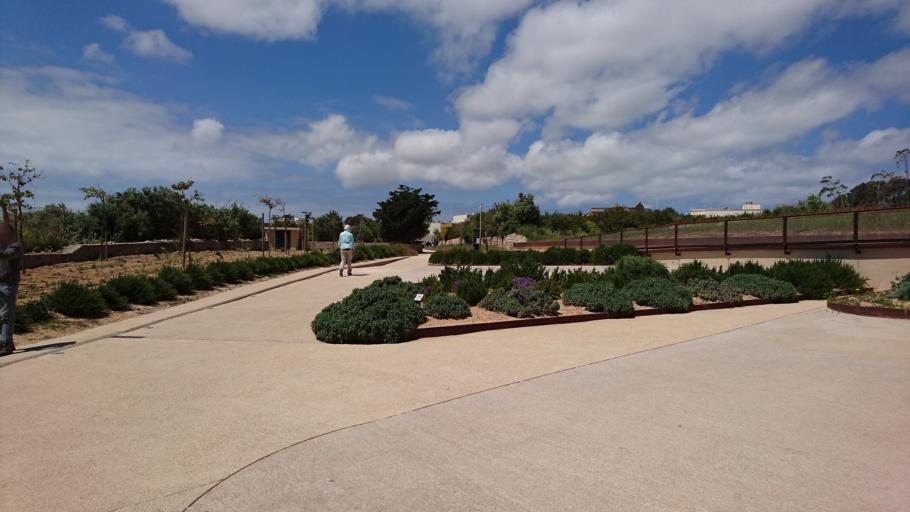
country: MT
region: Ix-Xaghra
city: Xaghra
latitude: 36.0474
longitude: 14.2686
